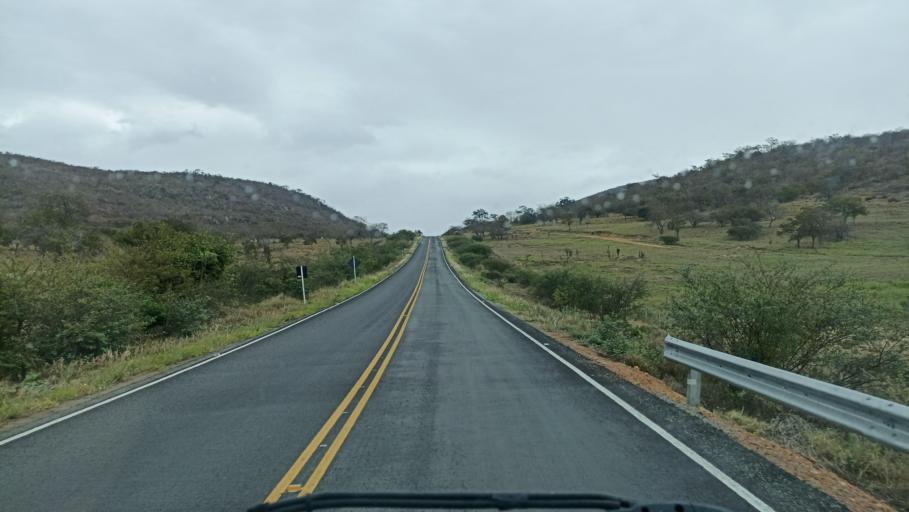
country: BR
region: Bahia
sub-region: Andarai
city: Vera Cruz
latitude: -13.0453
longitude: -40.7738
